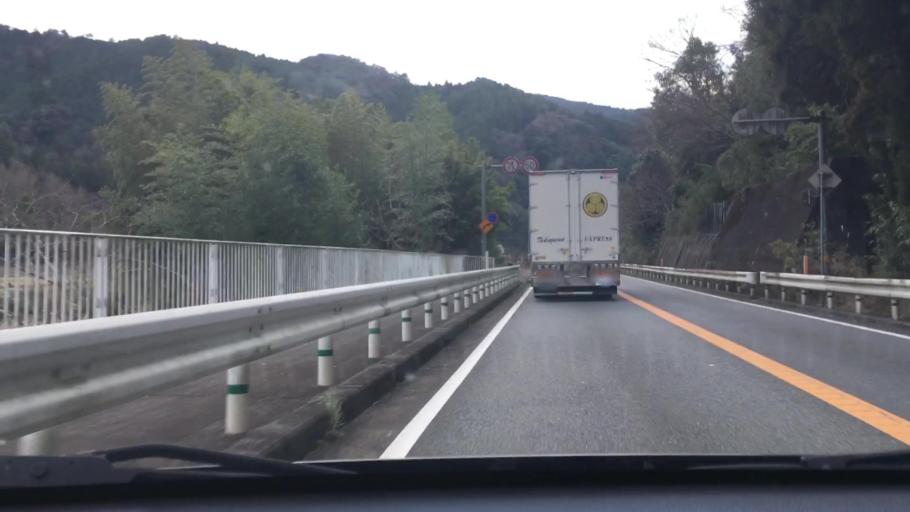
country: JP
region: Oita
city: Usuki
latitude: 33.0066
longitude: 131.7376
